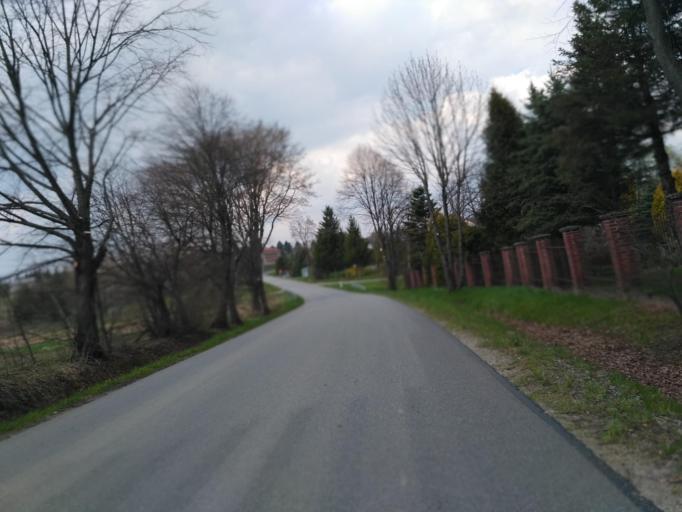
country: PL
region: Subcarpathian Voivodeship
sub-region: Powiat sanocki
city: Strachocina
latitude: 49.5999
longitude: 22.0962
